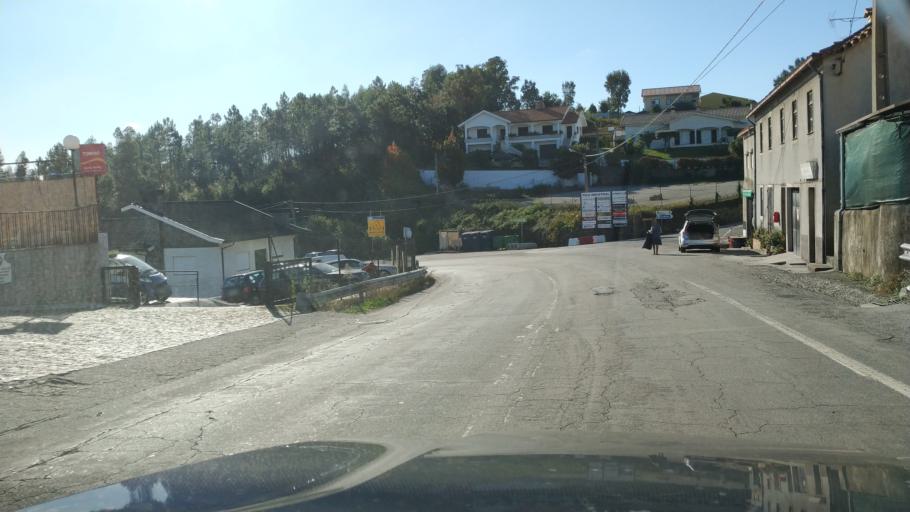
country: PT
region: Aveiro
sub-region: Vale de Cambra
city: Vale de Cambra
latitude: 40.8729
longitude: -8.4146
